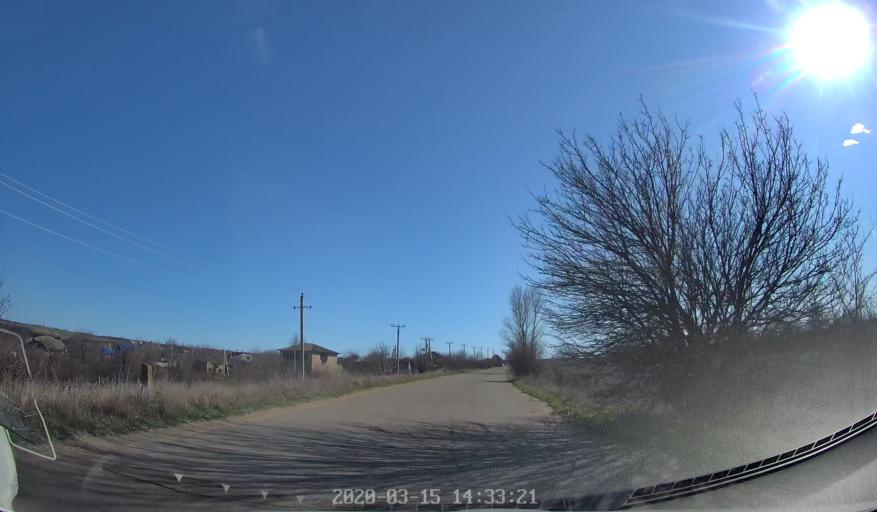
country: MD
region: Orhei
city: Orhei
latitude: 47.3382
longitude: 28.9169
